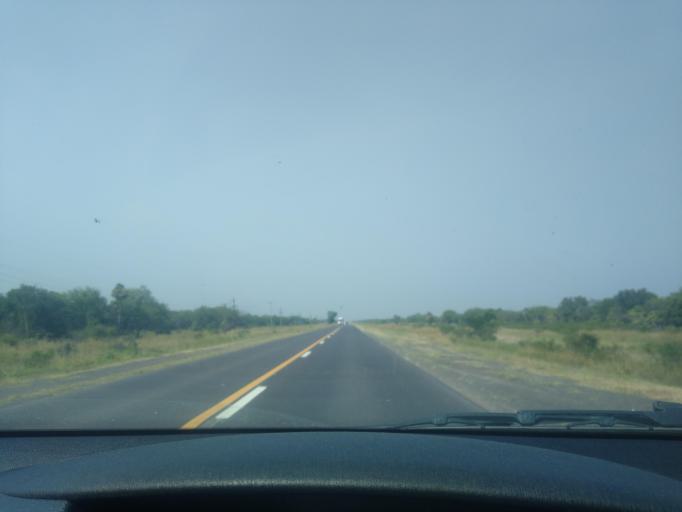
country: AR
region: Chaco
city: Fontana
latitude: -27.5411
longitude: -59.1297
